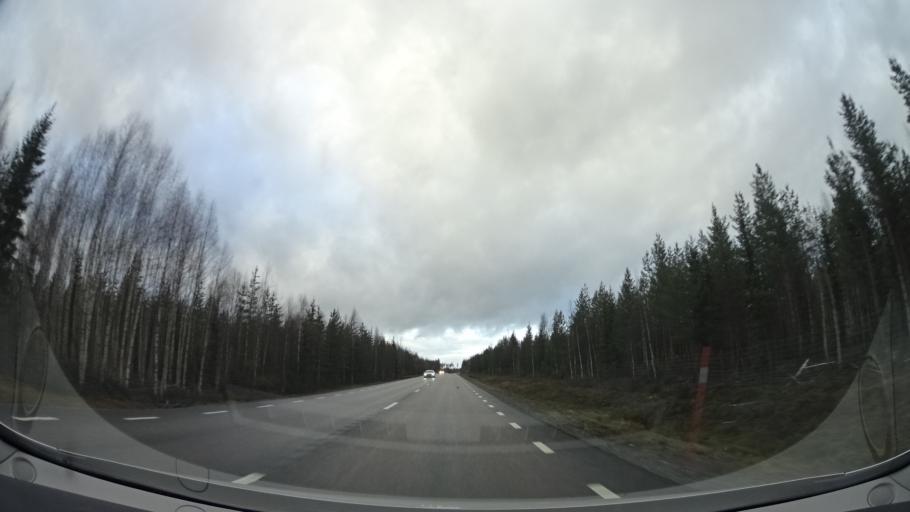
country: SE
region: Vaesterbotten
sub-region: Skelleftea Kommun
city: Viken
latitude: 64.7898
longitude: 20.7692
